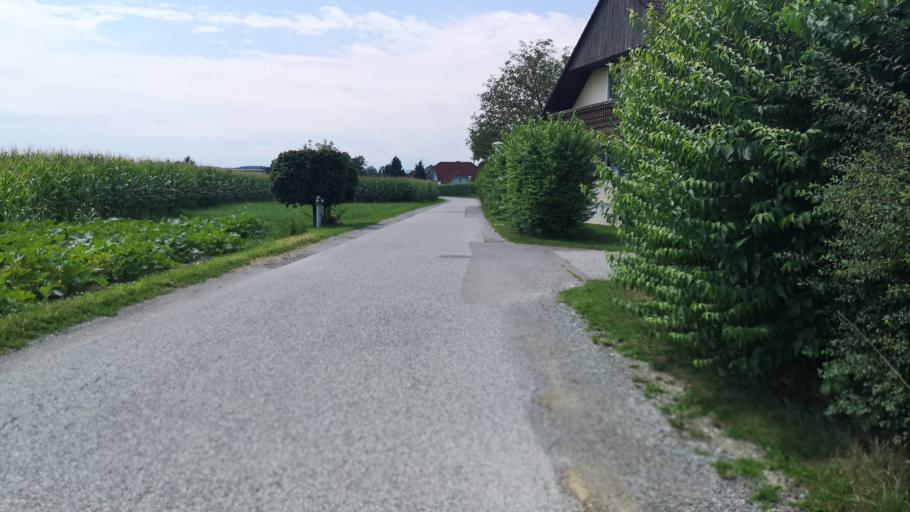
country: AT
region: Styria
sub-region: Politischer Bezirk Leibnitz
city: Weitendorf
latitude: 46.9036
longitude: 15.4774
